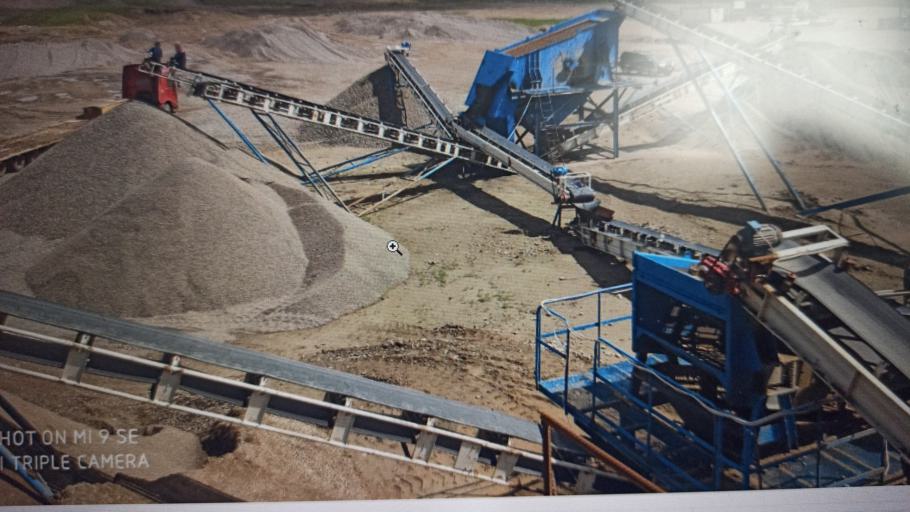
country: KG
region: Chuy
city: Bystrovka
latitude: 43.3243
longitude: 75.6859
